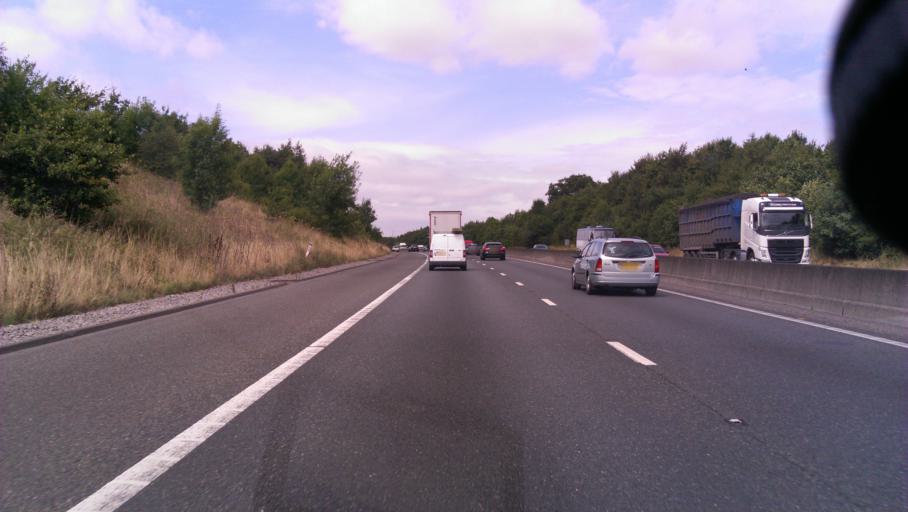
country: GB
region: England
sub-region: Essex
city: Elsenham
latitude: 51.9633
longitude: 0.2139
